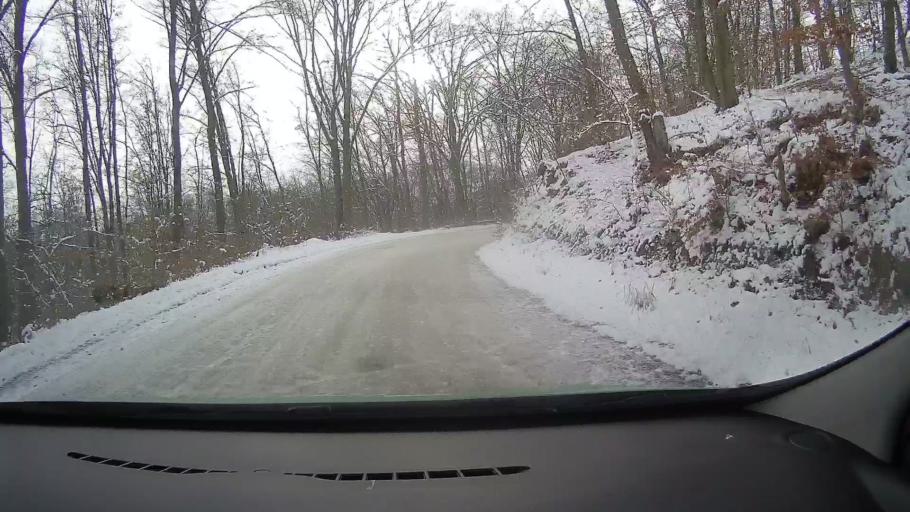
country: RO
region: Alba
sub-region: Comuna Almasu Mare
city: Almasu Mare
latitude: 46.0956
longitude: 23.1699
